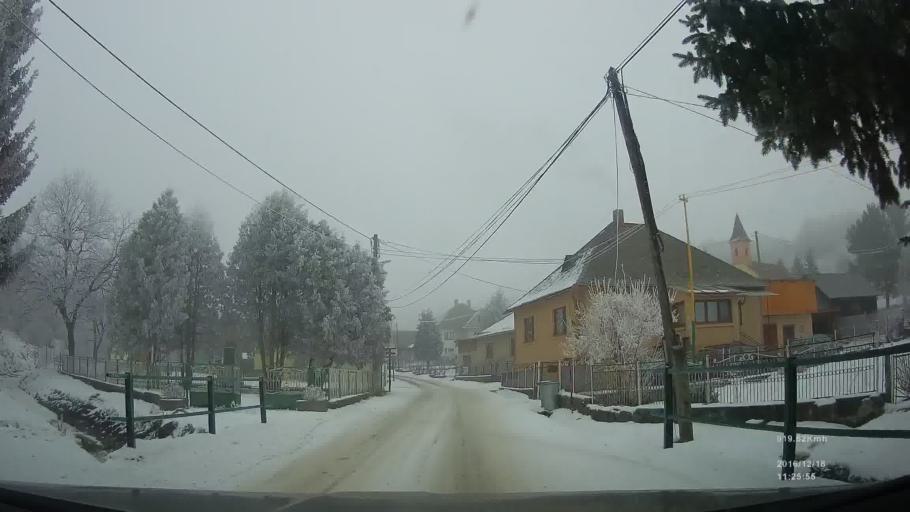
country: SK
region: Presovsky
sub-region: Okres Presov
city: Presov
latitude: 48.8982
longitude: 21.4068
